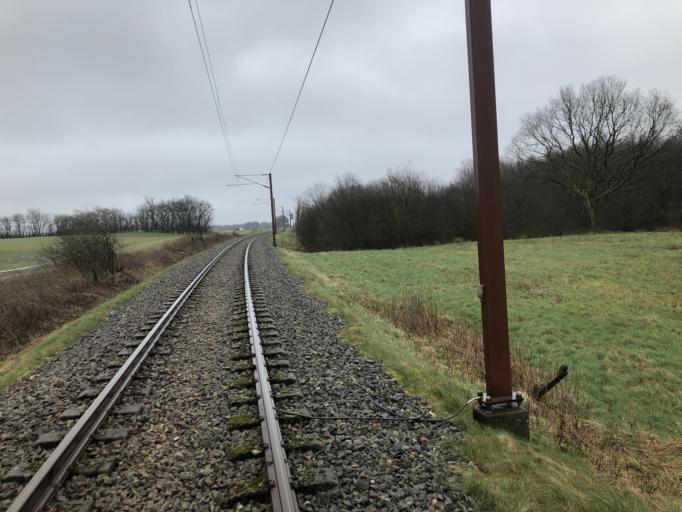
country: DK
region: South Denmark
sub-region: Aabenraa Kommune
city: Krusa
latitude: 54.9230
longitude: 9.4592
